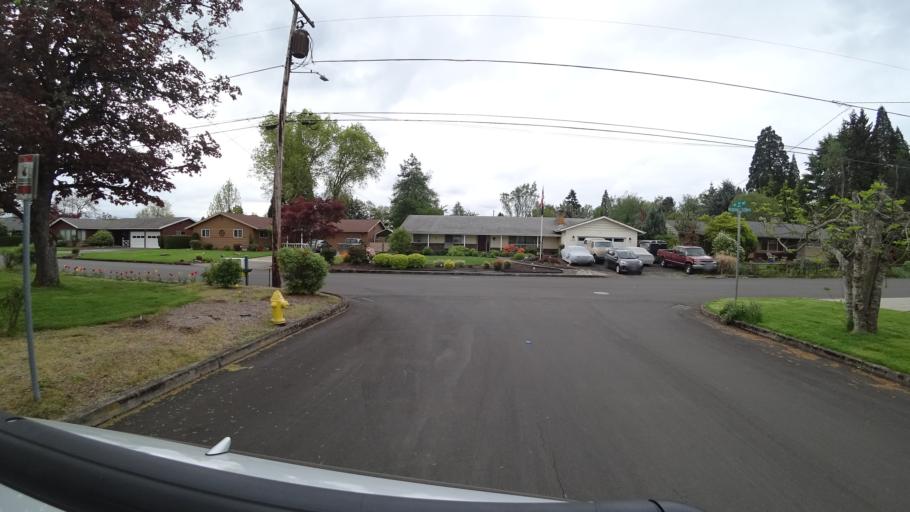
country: US
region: Oregon
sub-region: Washington County
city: Hillsboro
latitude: 45.5294
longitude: -122.9761
